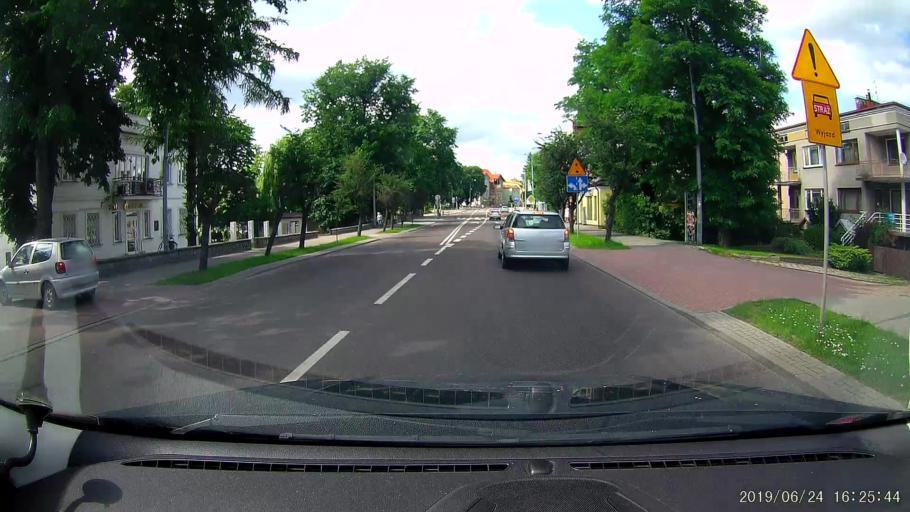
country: PL
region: Lublin Voivodeship
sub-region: Powiat tomaszowski
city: Tomaszow Lubelski
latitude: 50.4456
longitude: 23.4167
